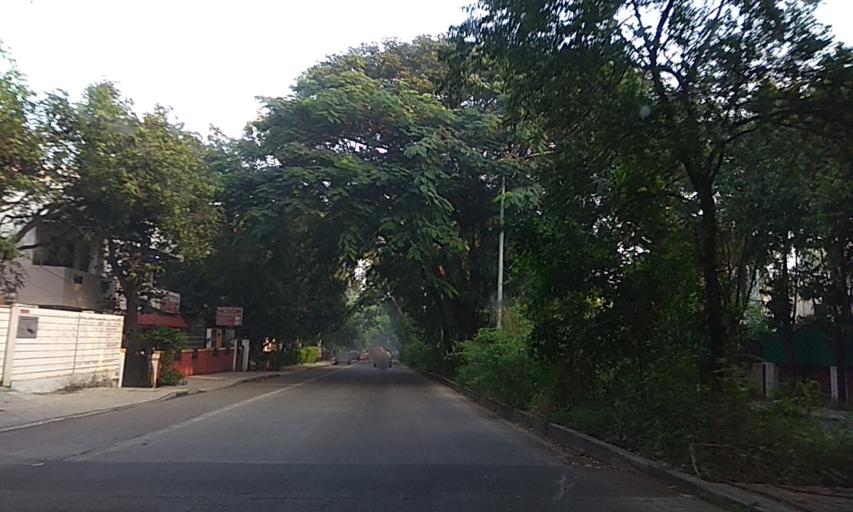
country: IN
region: Maharashtra
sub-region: Pune Division
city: Shivaji Nagar
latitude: 18.5426
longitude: 73.8174
